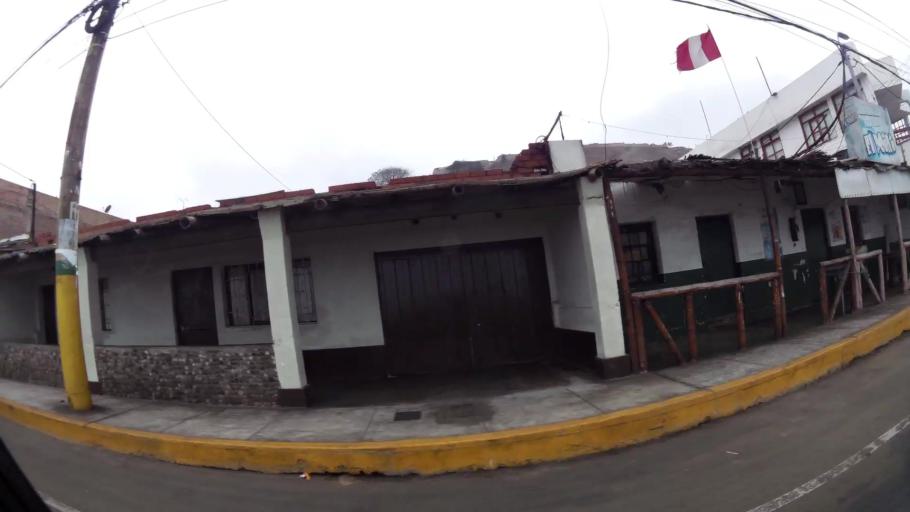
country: PE
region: Lima
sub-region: Barranca
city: Barranca
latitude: -10.7626
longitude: -77.7625
